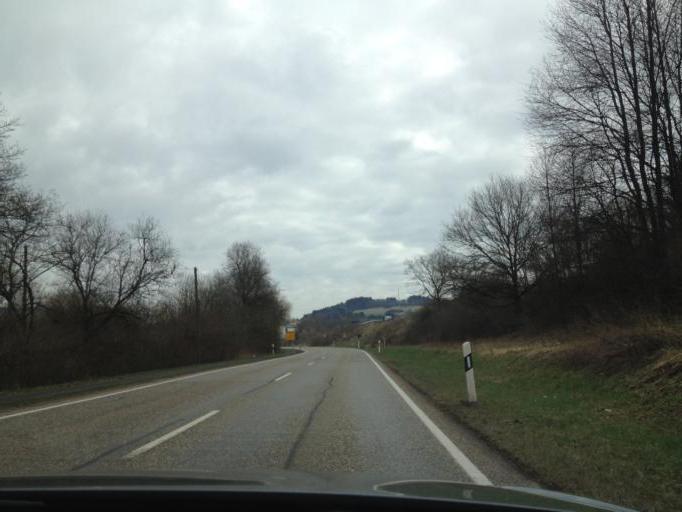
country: DE
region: Saarland
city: Freisen
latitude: 49.5534
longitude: 7.2354
